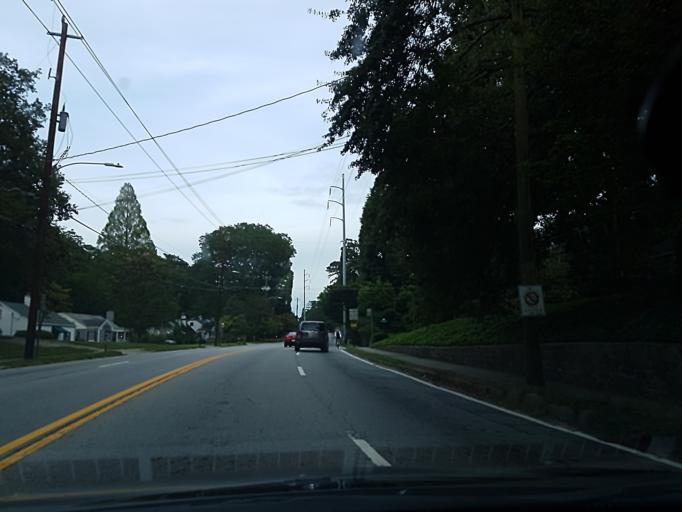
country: US
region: Georgia
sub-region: DeKalb County
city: North Decatur
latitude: 33.7923
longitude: -84.3125
